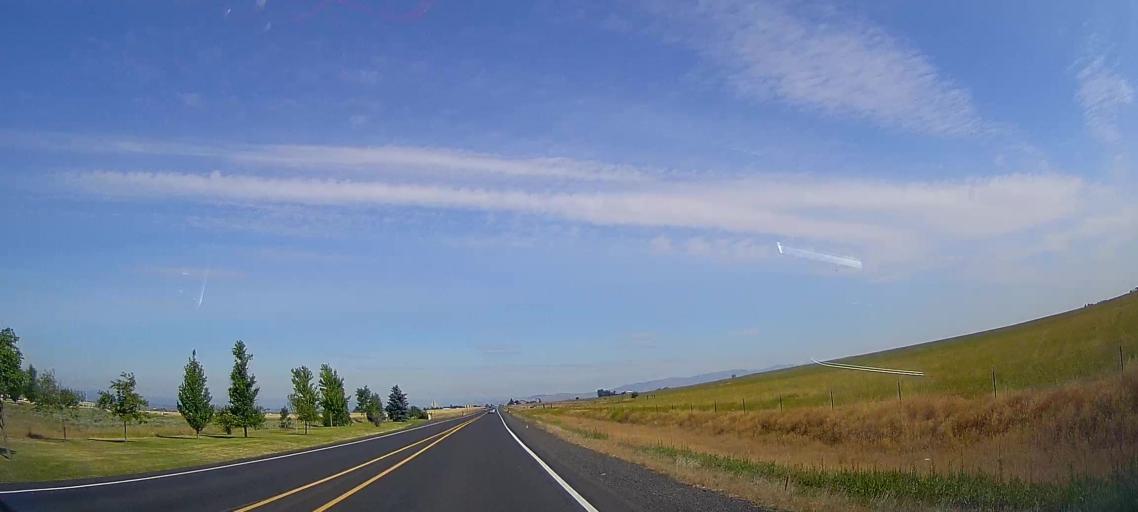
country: US
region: Oregon
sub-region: Jefferson County
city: Madras
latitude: 44.6671
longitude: -121.1382
